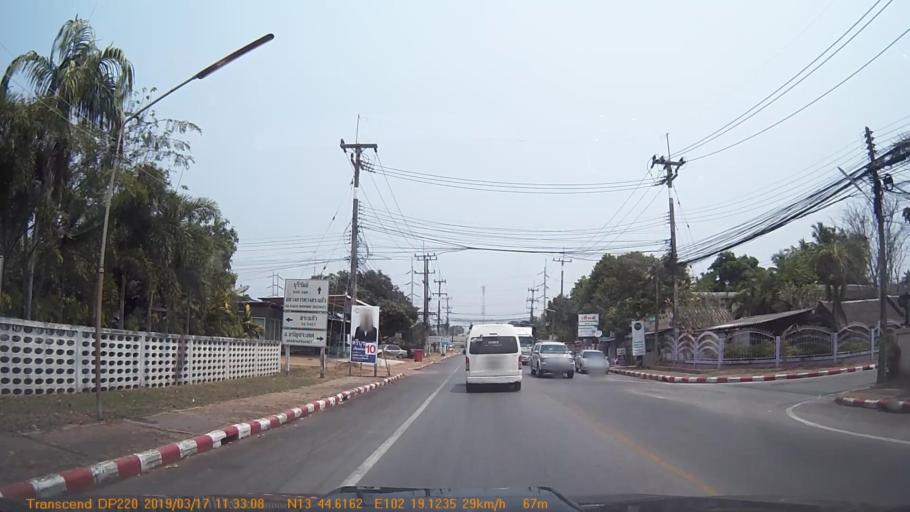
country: TH
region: Sa Kaeo
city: Watthana Nakhon
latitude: 13.7437
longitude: 102.3188
